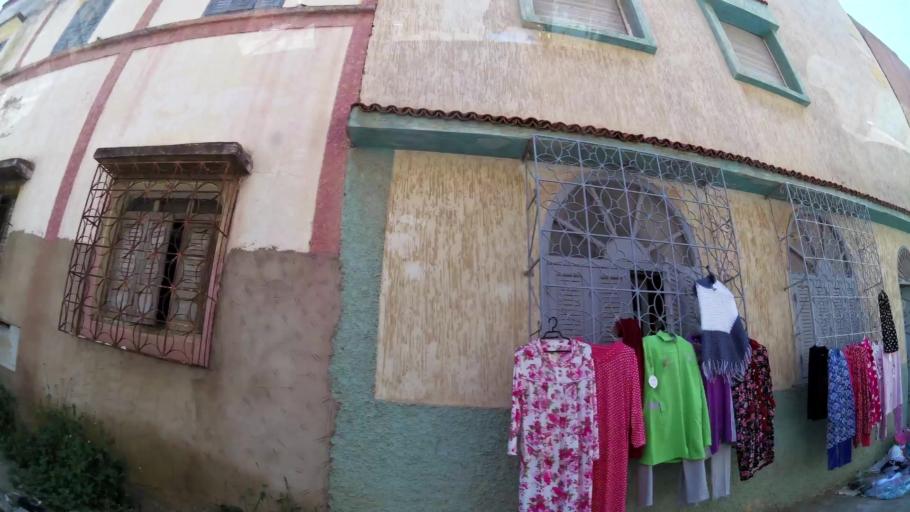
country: MA
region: Rabat-Sale-Zemmour-Zaer
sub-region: Khemisset
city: Khemisset
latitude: 33.8127
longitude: -6.0738
